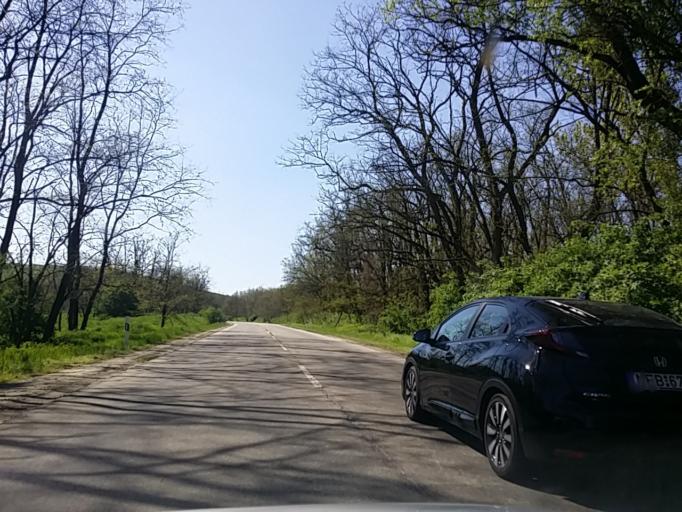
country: HU
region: Pest
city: Domony
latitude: 47.6125
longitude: 19.4070
